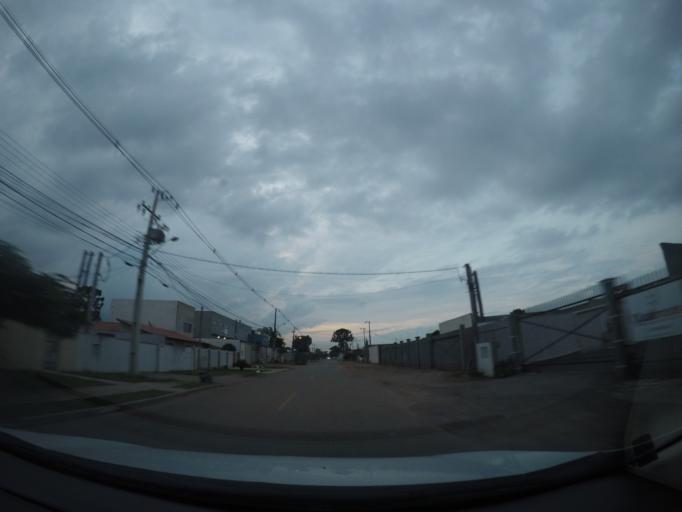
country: BR
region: Parana
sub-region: Sao Jose Dos Pinhais
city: Sao Jose dos Pinhais
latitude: -25.5087
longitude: -49.2257
